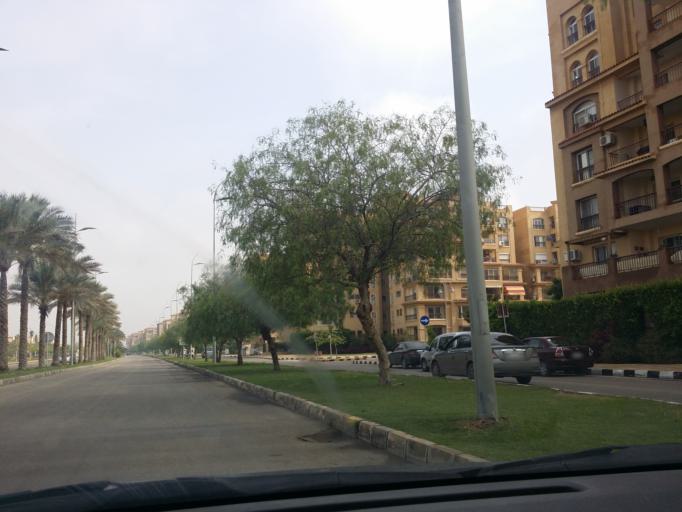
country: EG
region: Muhafazat al Qalyubiyah
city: Al Khankah
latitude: 30.0970
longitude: 31.6350
